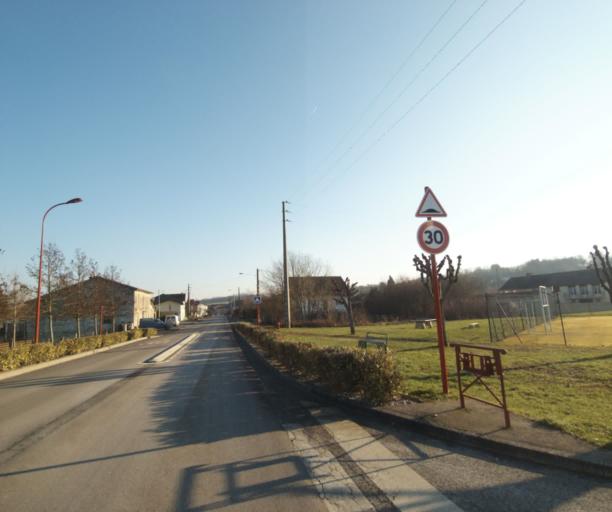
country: FR
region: Champagne-Ardenne
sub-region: Departement de la Haute-Marne
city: Bienville
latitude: 48.5639
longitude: 5.0485
